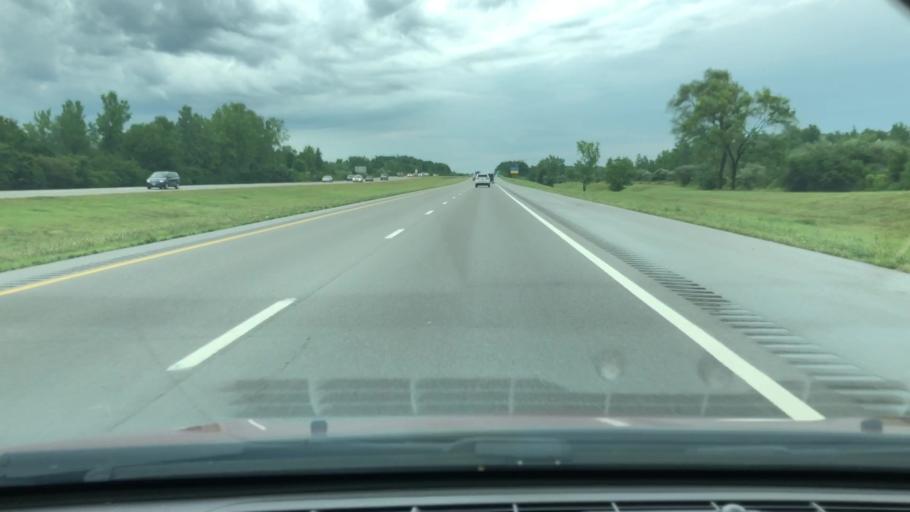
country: US
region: Ohio
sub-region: Greene County
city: Fairborn
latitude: 39.7989
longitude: -84.0018
